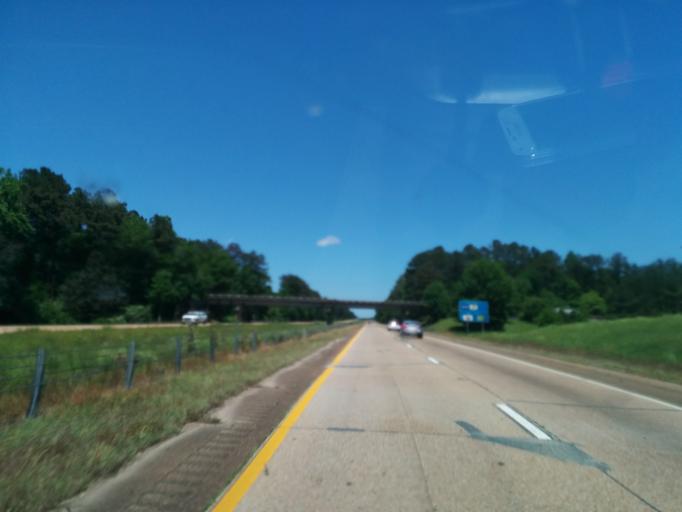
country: US
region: Mississippi
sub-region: Pike County
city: Magnolia
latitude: 31.1316
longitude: -90.4819
